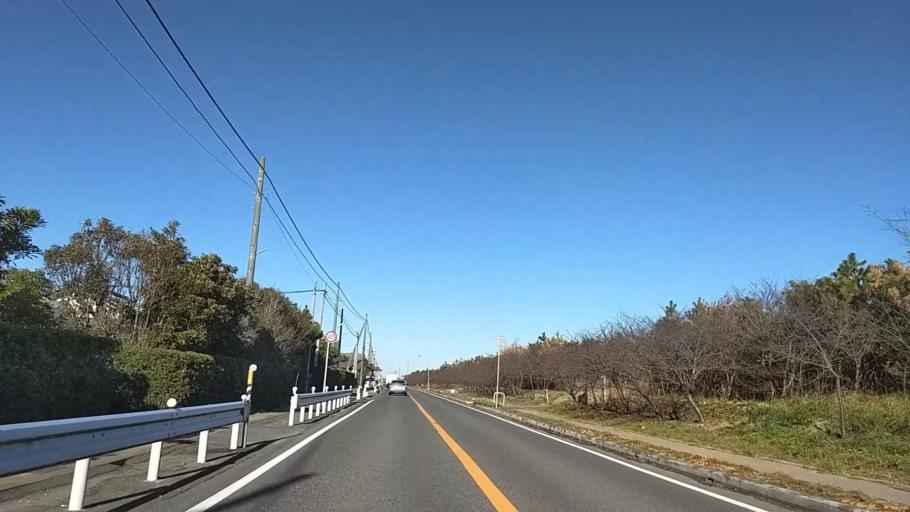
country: JP
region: Chiba
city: Togane
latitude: 35.4652
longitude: 140.4097
